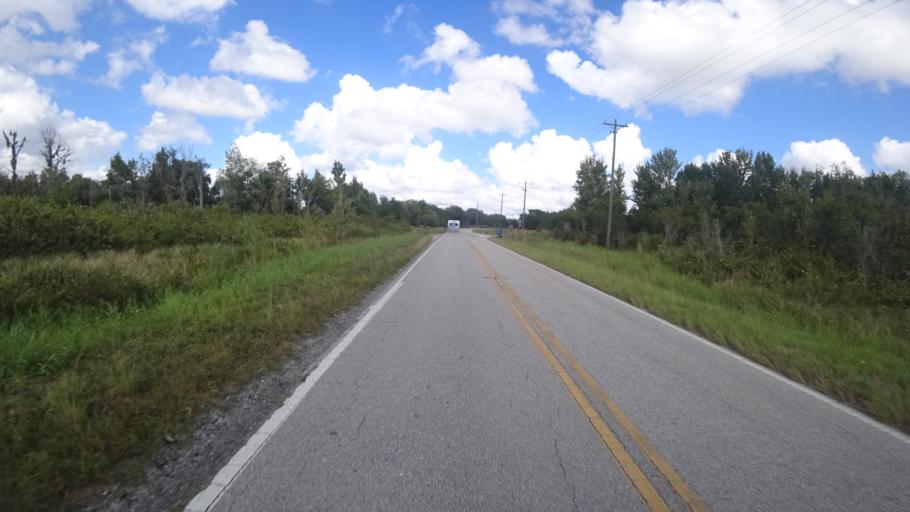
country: US
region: Florida
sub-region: Sarasota County
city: Lake Sarasota
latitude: 27.4068
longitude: -82.1330
